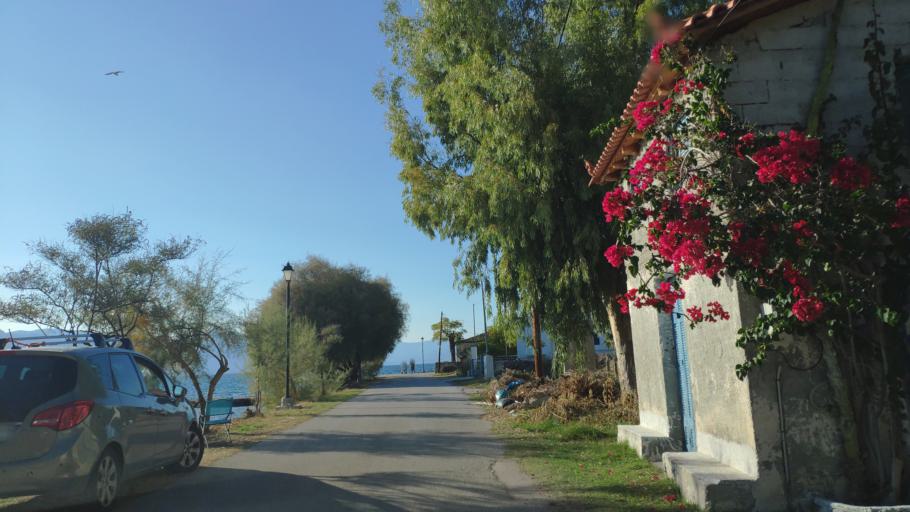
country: GR
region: Attica
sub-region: Nomos Piraios
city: Megalochori
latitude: 37.5909
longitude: 23.3412
